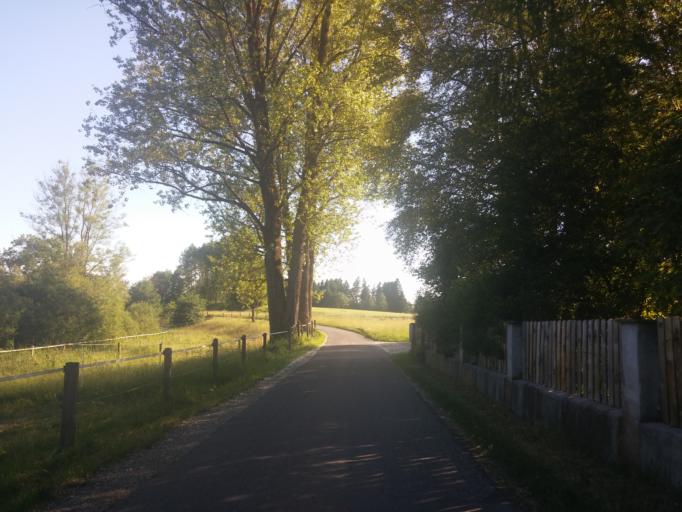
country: DE
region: Baden-Wuerttemberg
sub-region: Tuebingen Region
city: Kisslegg
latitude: 47.7803
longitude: 9.8719
